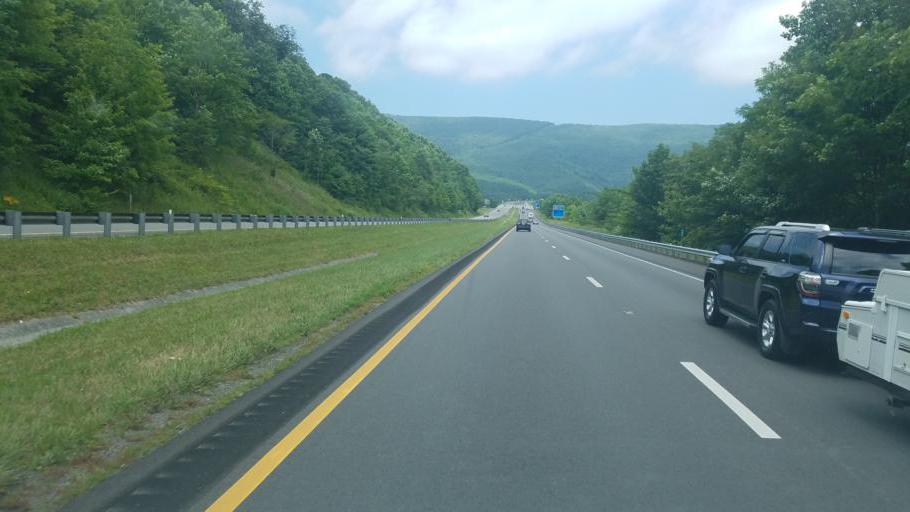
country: US
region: West Virginia
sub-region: Mercer County
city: Bluefield
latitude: 37.2487
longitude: -81.1149
